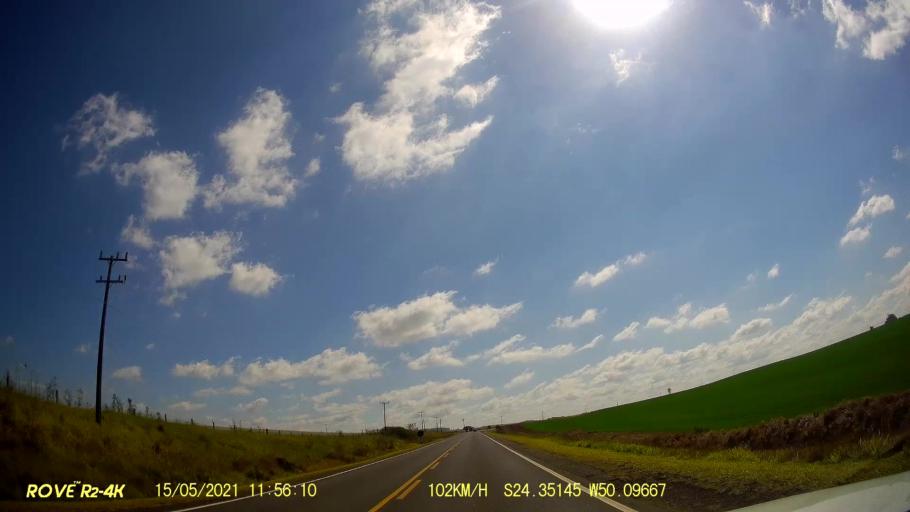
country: BR
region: Parana
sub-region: Pirai Do Sul
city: Pirai do Sul
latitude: -24.3518
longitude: -50.0970
